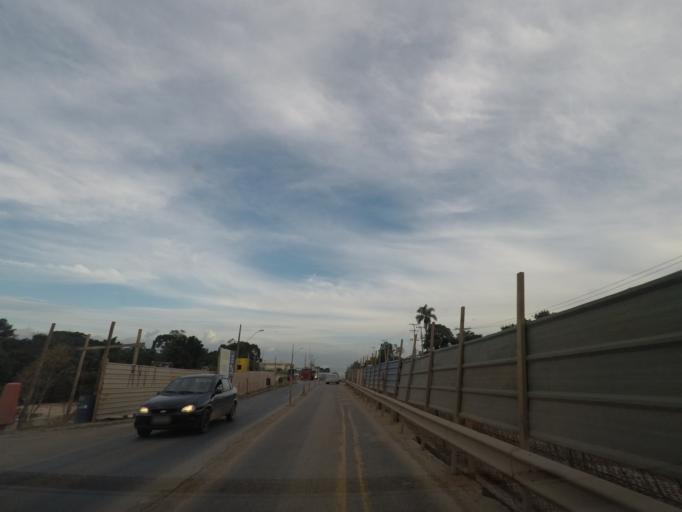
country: BR
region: Parana
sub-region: Colombo
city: Colombo
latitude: -25.3274
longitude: -49.2212
